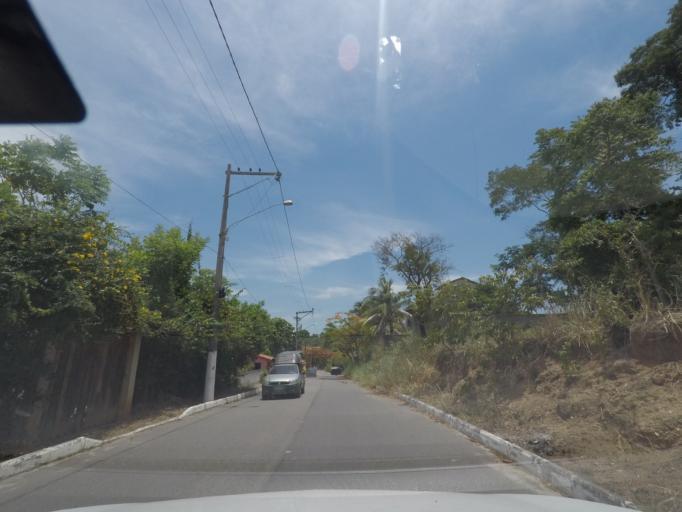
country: BR
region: Rio de Janeiro
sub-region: Marica
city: Marica
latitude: -22.9292
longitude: -42.8243
